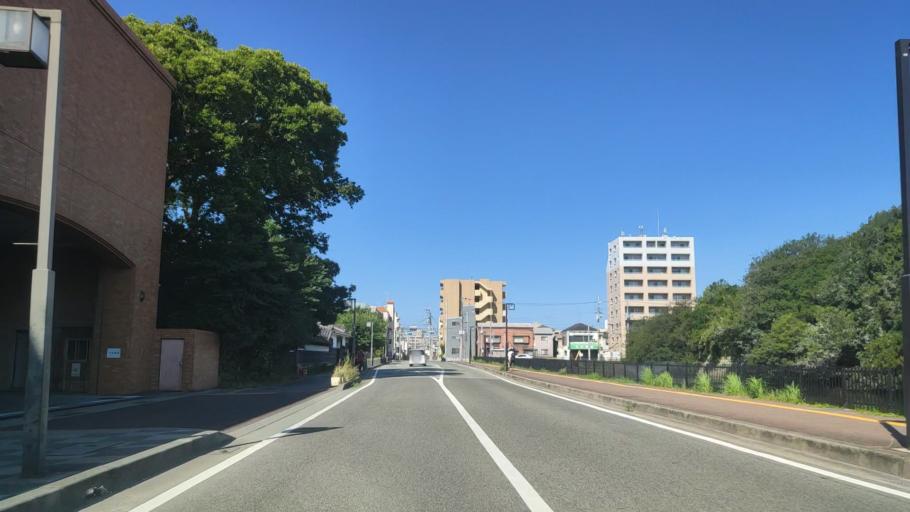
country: JP
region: Hyogo
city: Akashi
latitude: 34.6501
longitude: 134.9895
